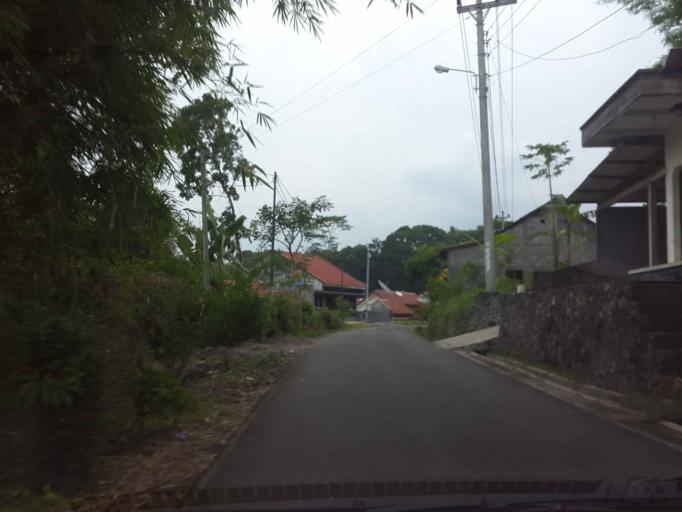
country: ID
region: Central Java
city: Salatiga
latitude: -7.3113
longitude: 110.5018
